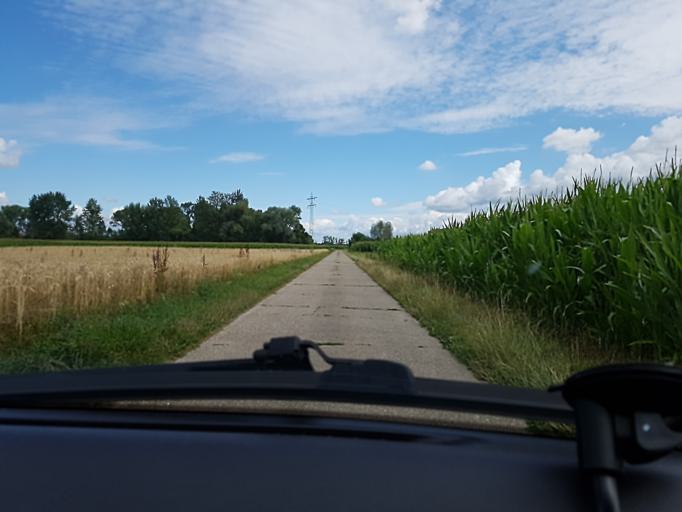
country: DE
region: Baden-Wuerttemberg
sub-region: Freiburg Region
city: Kehl
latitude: 48.5769
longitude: 7.8576
